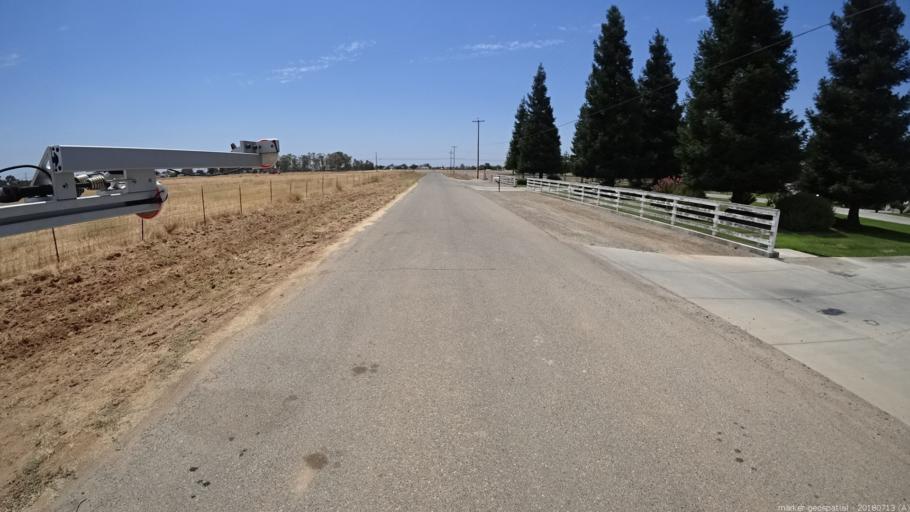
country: US
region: California
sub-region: Madera County
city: Madera Acres
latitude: 36.9980
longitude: -120.0675
